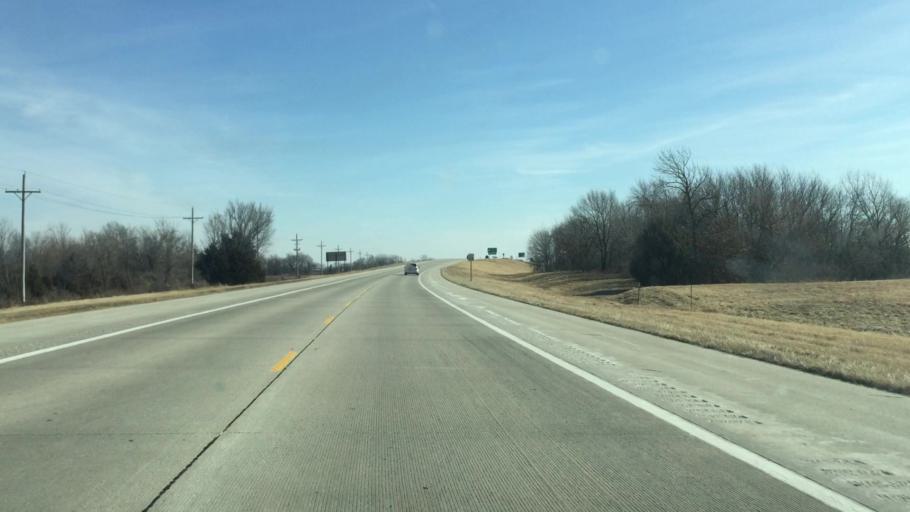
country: US
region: Kansas
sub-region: Labette County
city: Parsons
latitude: 37.3700
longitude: -95.2827
